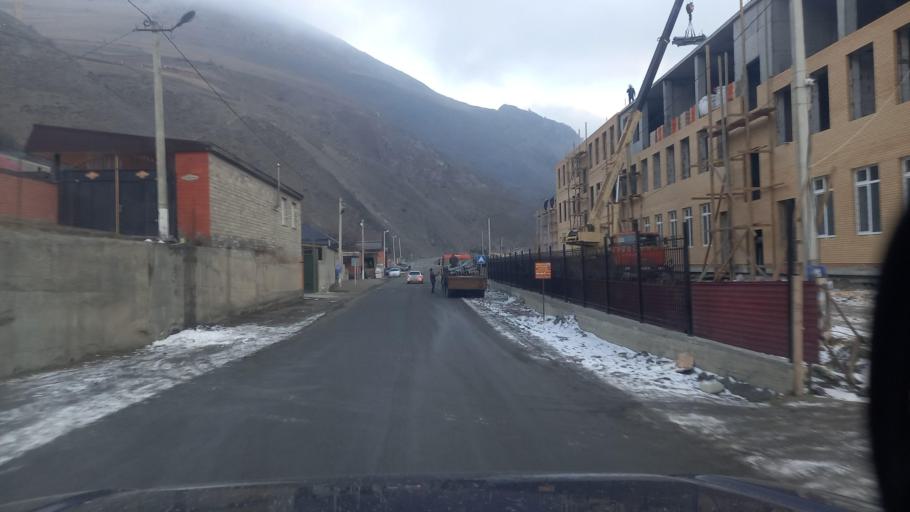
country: RU
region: Ingushetiya
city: Dzhayrakh
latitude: 42.8024
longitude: 44.7543
